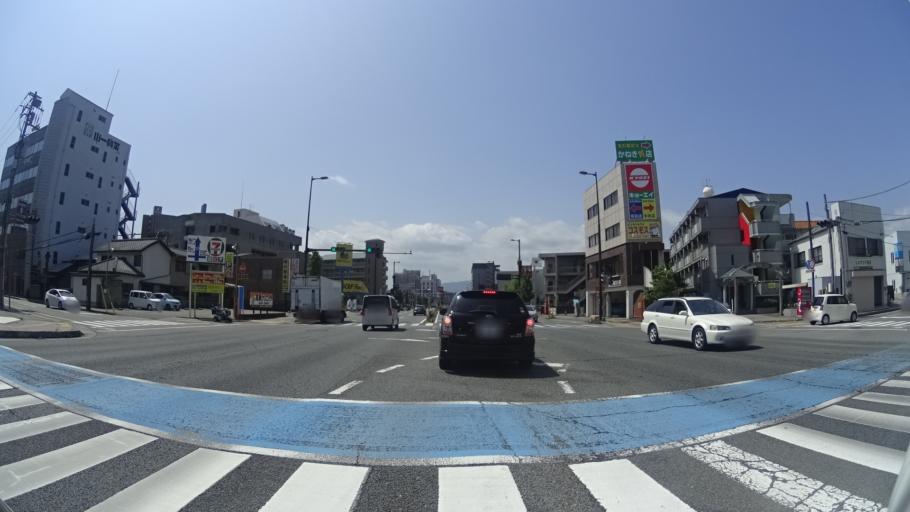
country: JP
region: Tokushima
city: Tokushima-shi
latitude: 34.0619
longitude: 134.5559
